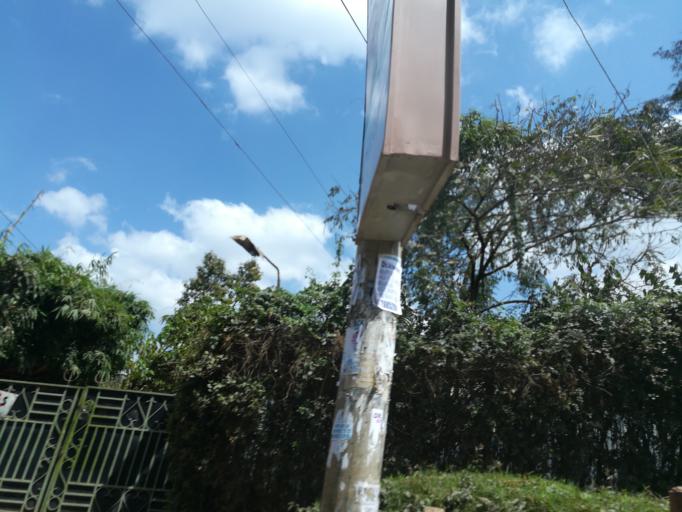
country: KE
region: Nairobi Area
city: Nairobi
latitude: -1.2926
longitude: 36.7859
